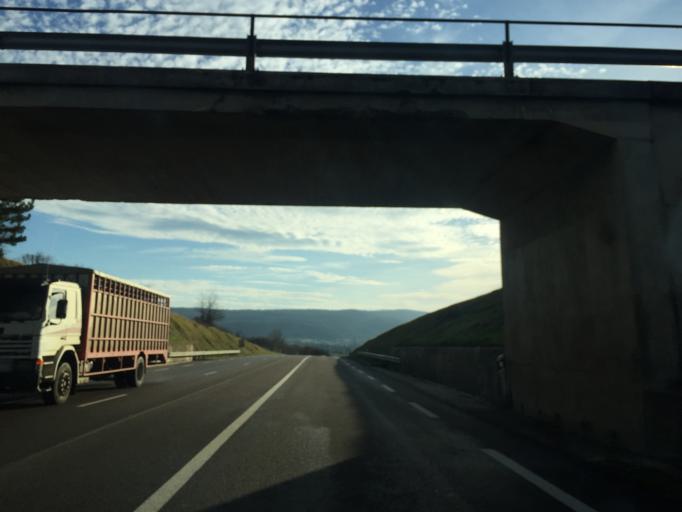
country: FR
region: Franche-Comte
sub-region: Departement du Jura
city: Arbois
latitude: 46.9298
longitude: 5.7758
